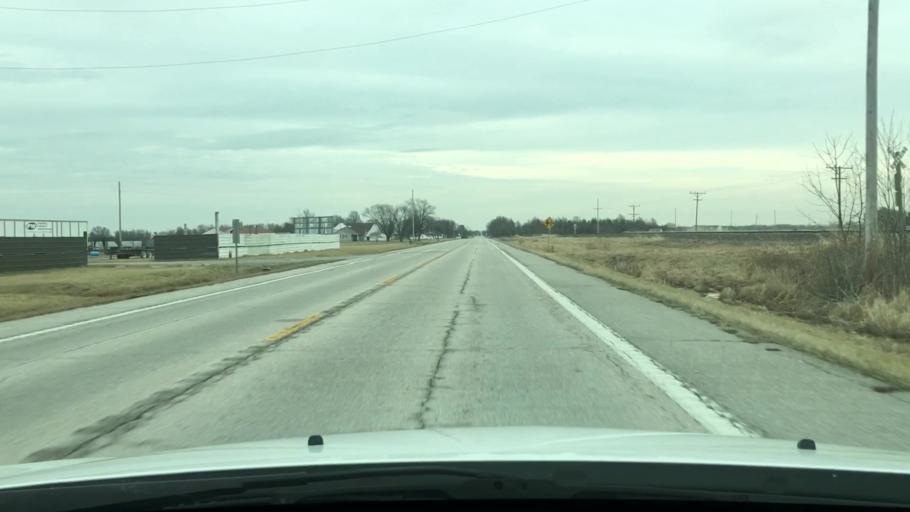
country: US
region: Missouri
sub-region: Audrain County
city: Vandalia
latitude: 39.2918
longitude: -91.5298
